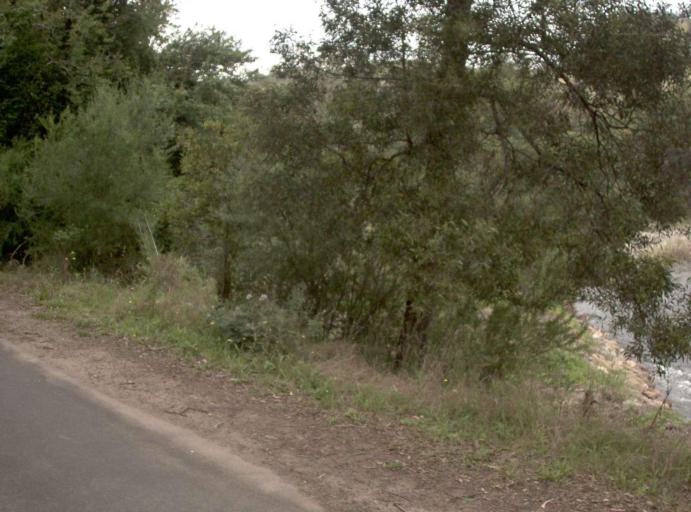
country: AU
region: Victoria
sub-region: East Gippsland
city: Bairnsdale
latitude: -37.4548
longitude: 147.2514
